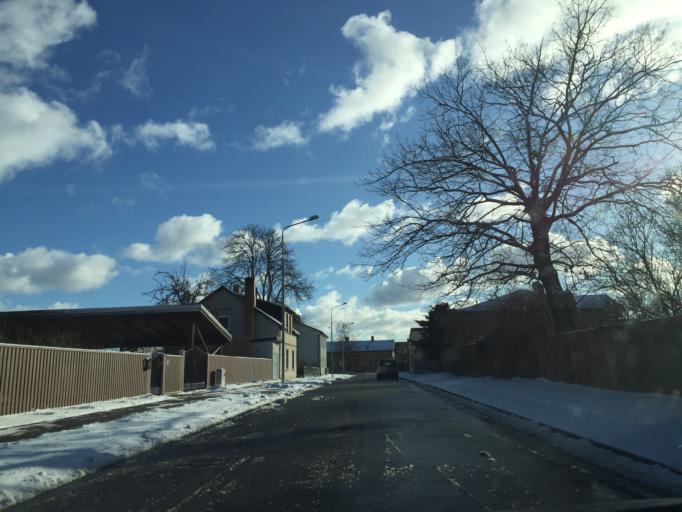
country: LV
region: Ventspils
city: Ventspils
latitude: 57.3866
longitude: 21.5580
